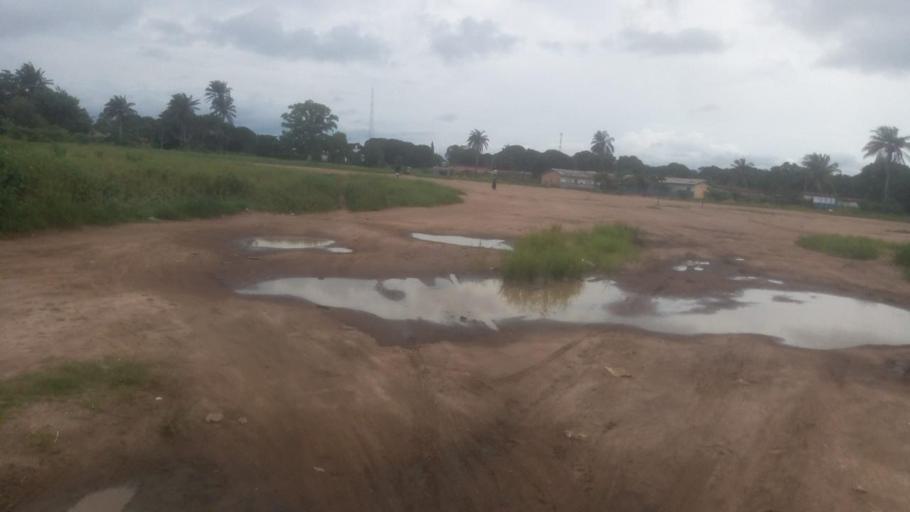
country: SL
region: Northern Province
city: Masoyila
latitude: 8.6084
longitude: -13.1868
